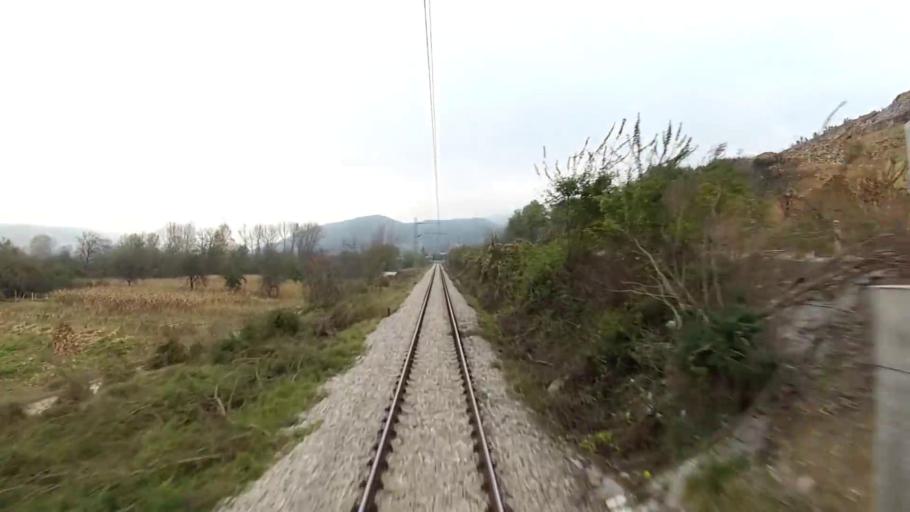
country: RS
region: Central Serbia
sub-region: Pirotski Okrug
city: Dimitrovgrad
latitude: 43.0064
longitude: 22.8058
